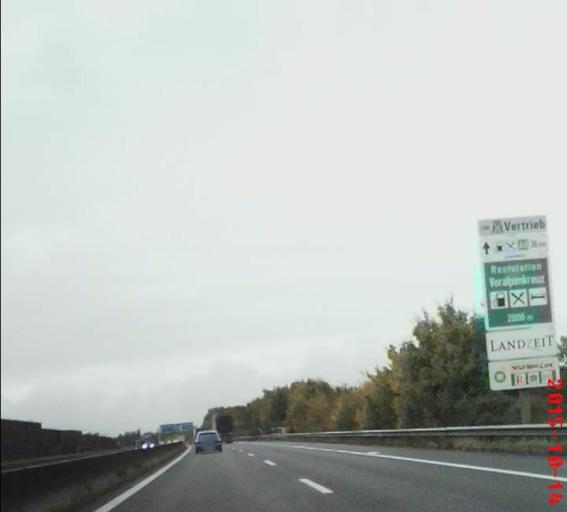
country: AT
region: Upper Austria
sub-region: Wels-Land
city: Sattledt
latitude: 48.0466
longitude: 14.0560
